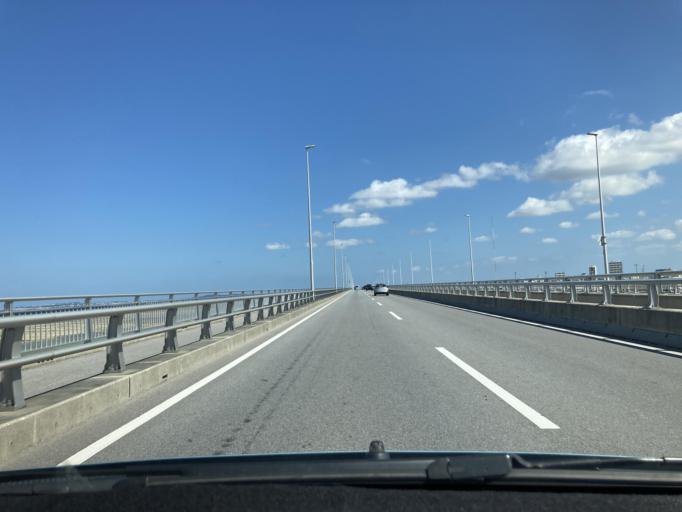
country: JP
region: Okinawa
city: Naha-shi
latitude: 26.2664
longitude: 127.7014
